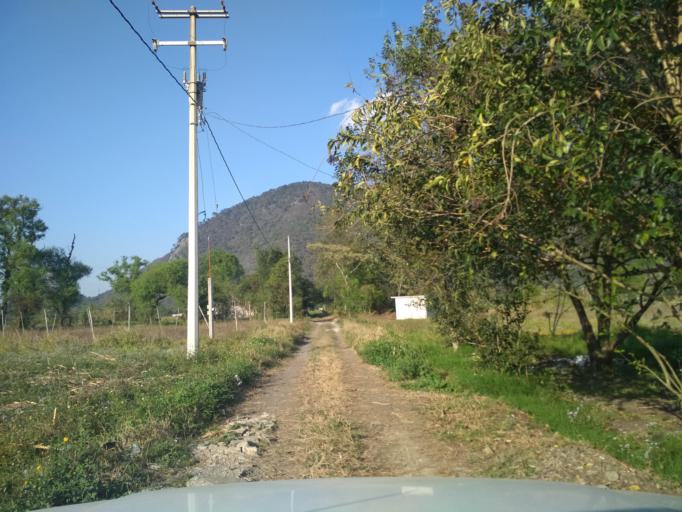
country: MX
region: Veracruz
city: Jalapilla
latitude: 18.8197
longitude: -97.0745
